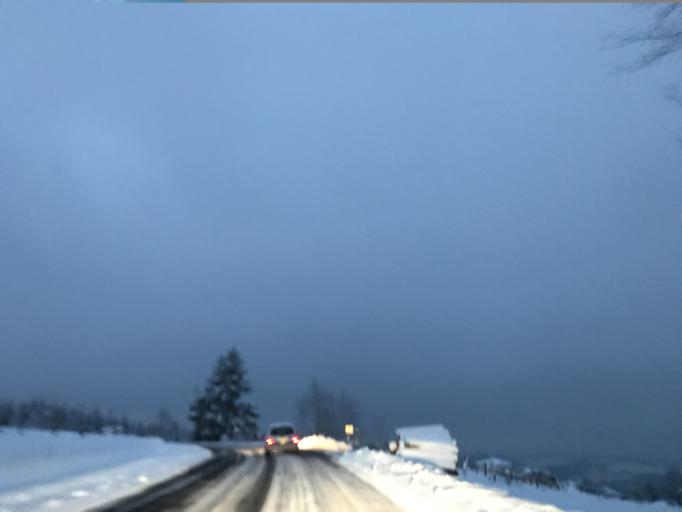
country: FR
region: Auvergne
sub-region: Departement du Puy-de-Dome
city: Courpiere
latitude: 45.7219
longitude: 3.5853
